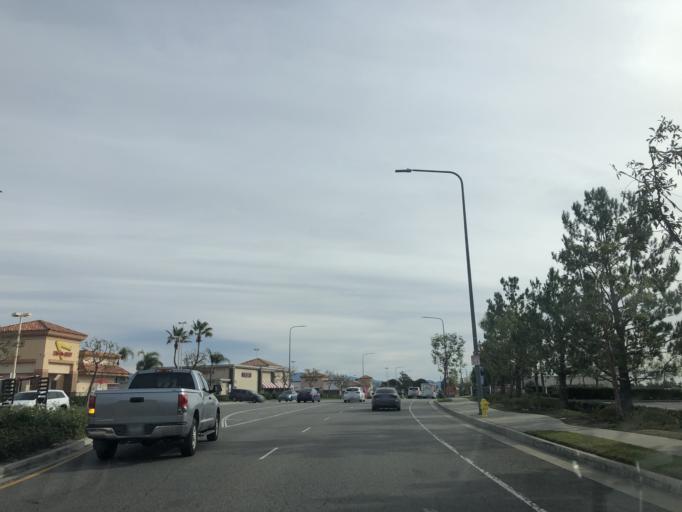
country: US
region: California
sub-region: Los Angeles County
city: Chatsworth
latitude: 34.2755
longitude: -118.5690
